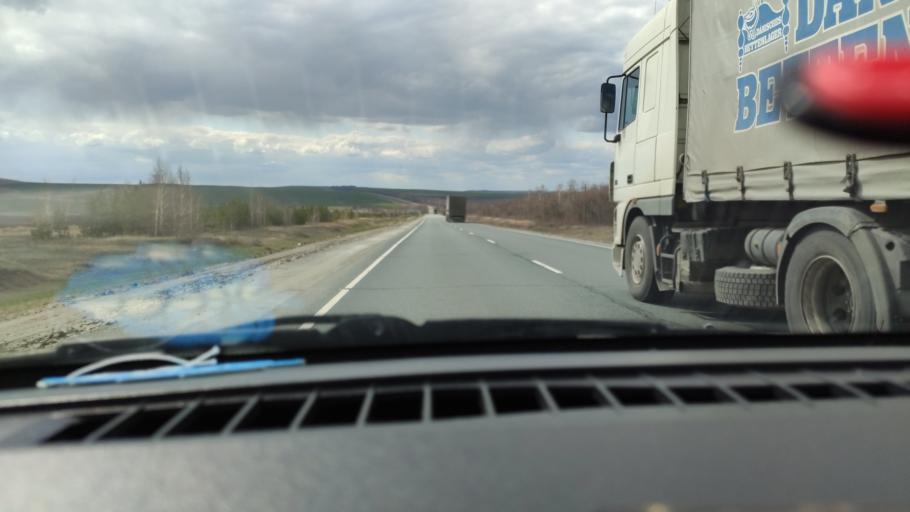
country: RU
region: Saratov
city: Alekseyevka
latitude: 52.2551
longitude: 47.9158
